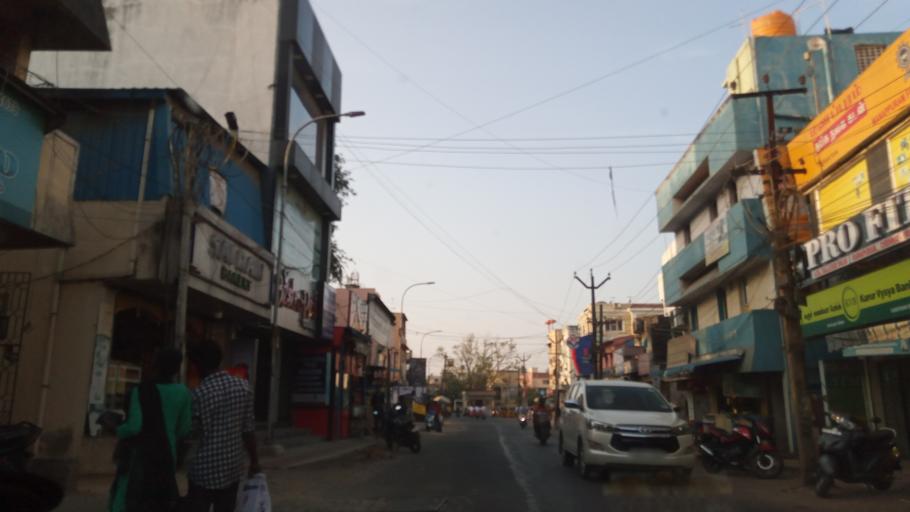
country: IN
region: Tamil Nadu
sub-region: Kancheepuram
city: Manappakkam
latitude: 13.0302
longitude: 80.1837
